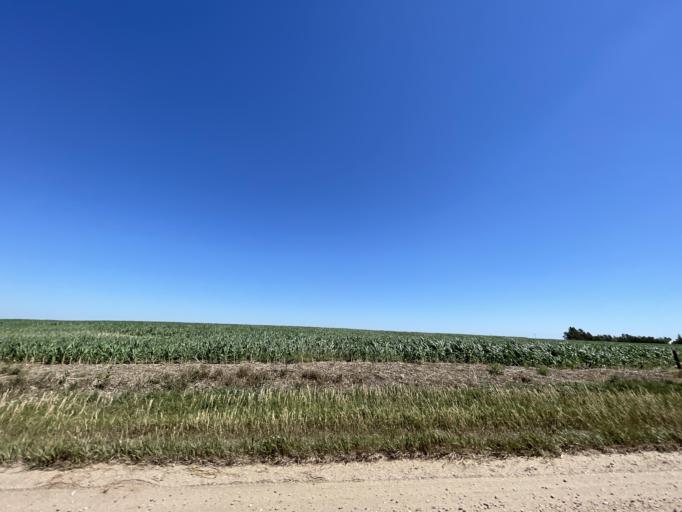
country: US
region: Nebraska
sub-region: Red Willow County
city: McCook
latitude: 40.4373
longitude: -100.6516
